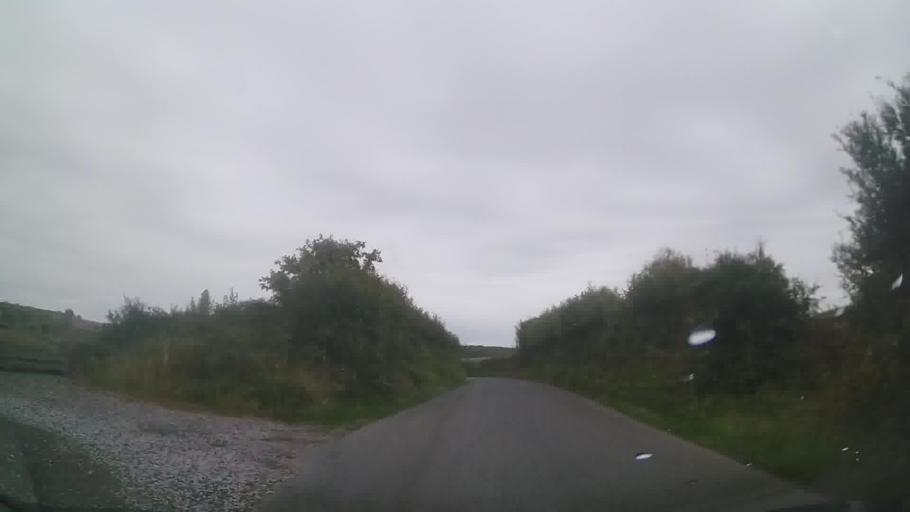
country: GB
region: Wales
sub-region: Pembrokeshire
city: Saundersfoot
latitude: 51.7357
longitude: -4.6386
